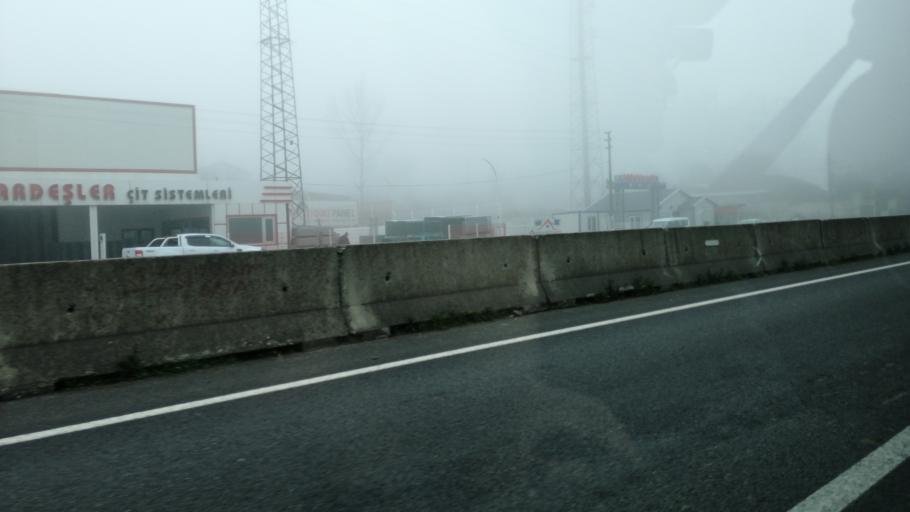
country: TR
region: Yalova
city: Ciftlikkoy
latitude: 40.6700
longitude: 29.3390
